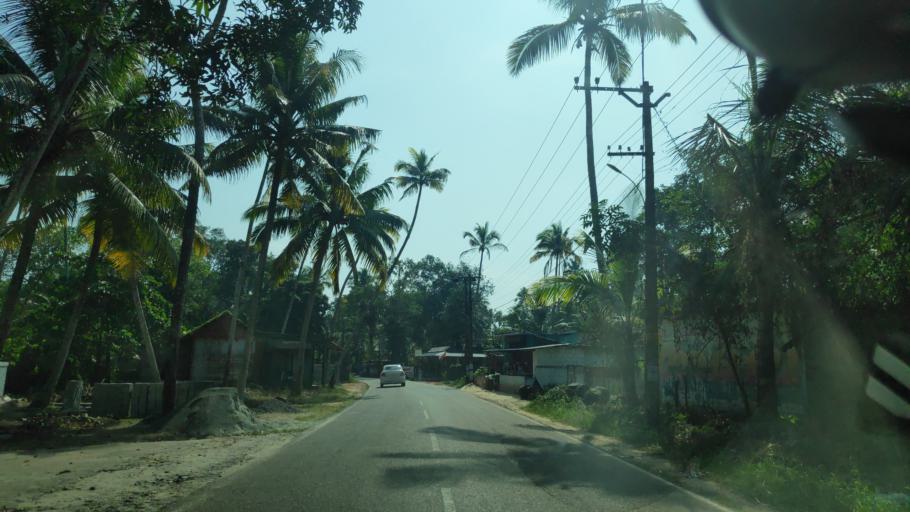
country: IN
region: Kerala
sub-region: Alappuzha
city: Vayalar
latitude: 9.6467
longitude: 76.2989
